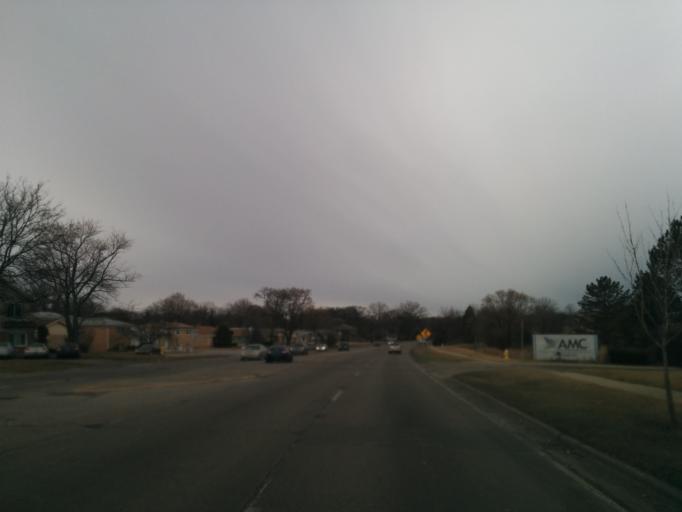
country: US
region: Illinois
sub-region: Cook County
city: Des Plaines
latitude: 42.0868
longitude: -87.8715
